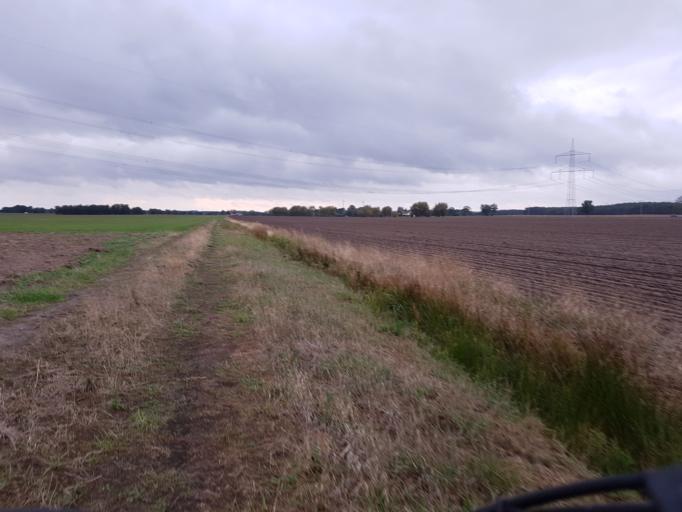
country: DE
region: Brandenburg
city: Schilda
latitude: 51.6105
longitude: 13.3719
